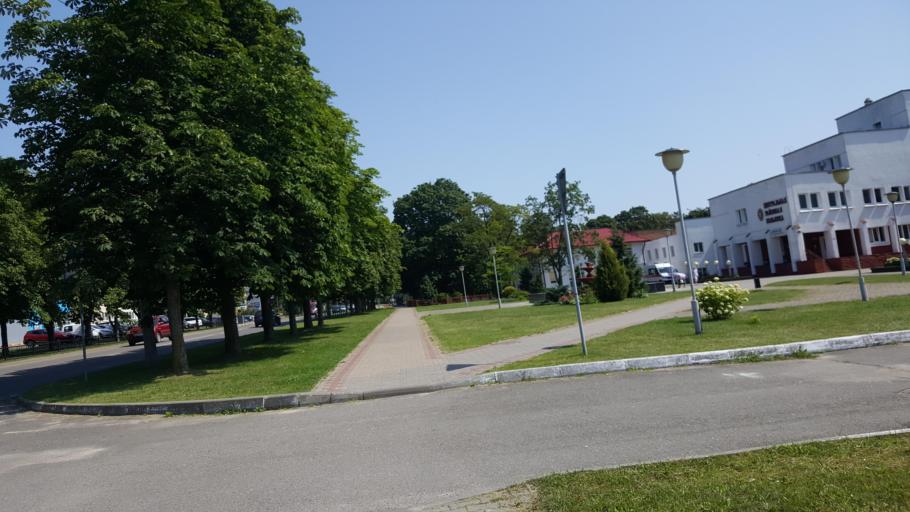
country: BY
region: Brest
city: Zhabinka
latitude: 52.1902
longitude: 24.0289
